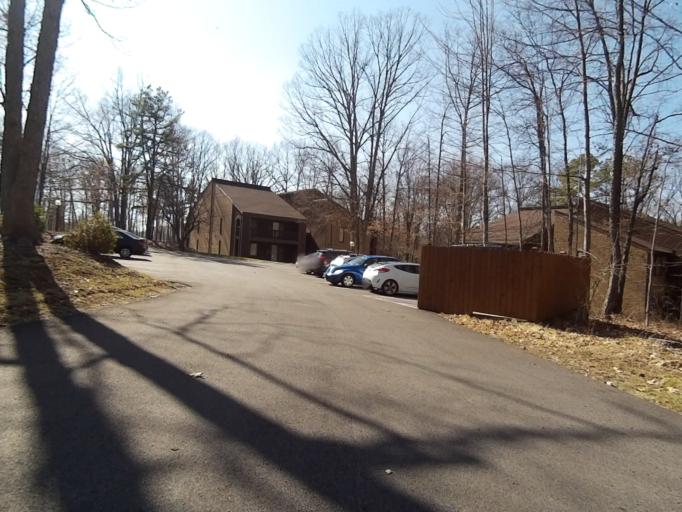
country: US
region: Pennsylvania
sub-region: Centre County
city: Park Forest Village
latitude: 40.8241
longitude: -77.8887
